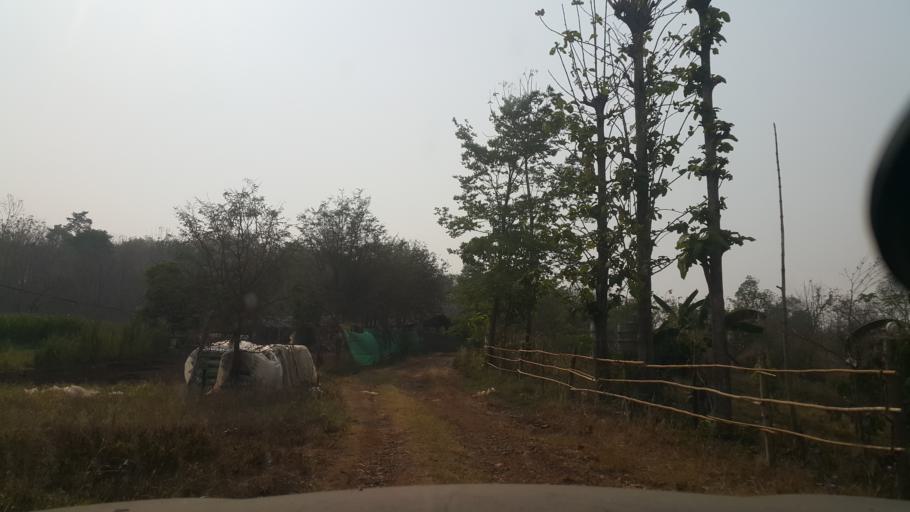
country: TH
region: Chiang Mai
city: Mae On
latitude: 18.7749
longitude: 99.2699
